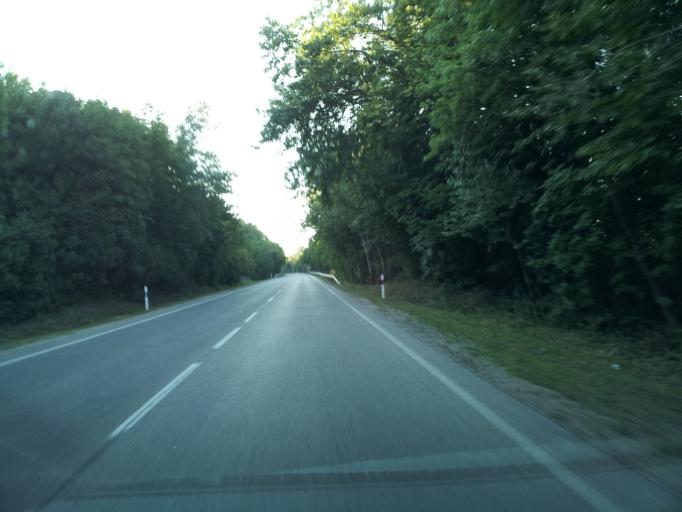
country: HU
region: Fejer
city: Szarliget
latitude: 47.5164
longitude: 18.4755
